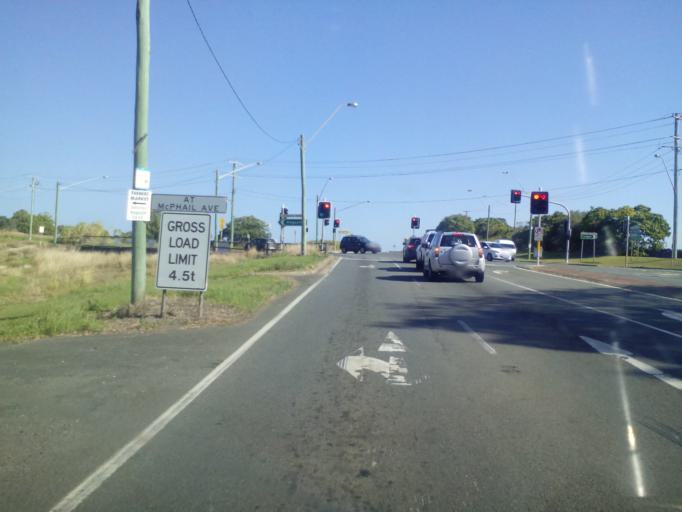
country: AU
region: New South Wales
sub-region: Tweed
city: Kingscliff
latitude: -28.2652
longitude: 153.5618
